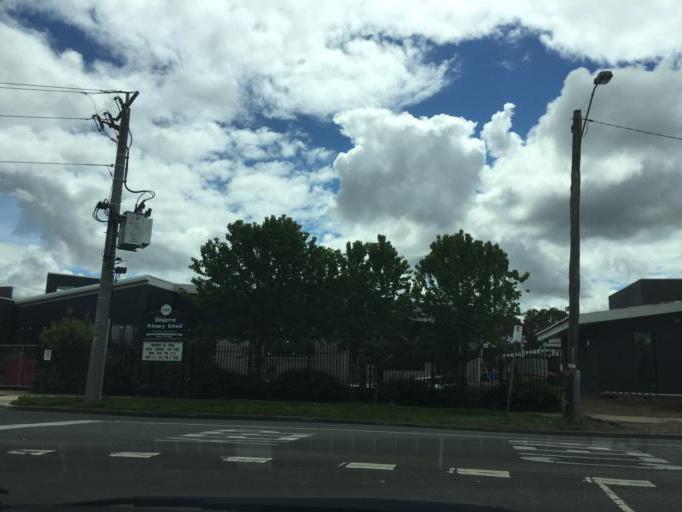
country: AU
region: Victoria
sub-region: Maribyrnong
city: Braybrook
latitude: -37.7924
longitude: 144.8567
